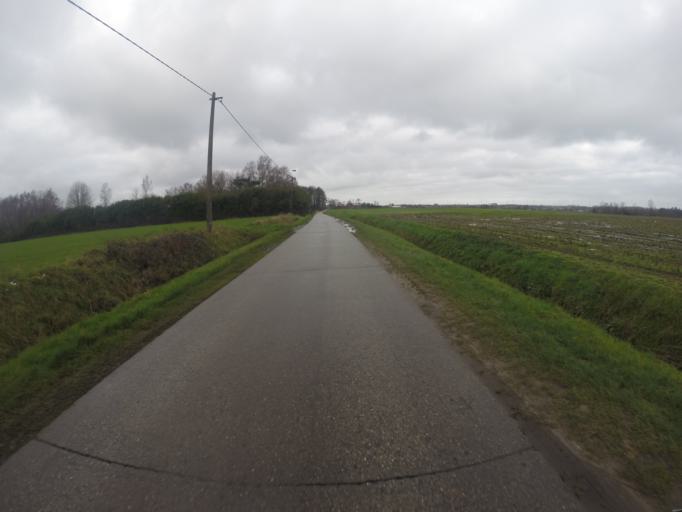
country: BE
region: Flanders
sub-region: Provincie Oost-Vlaanderen
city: Eeklo
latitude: 51.1661
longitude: 3.4978
